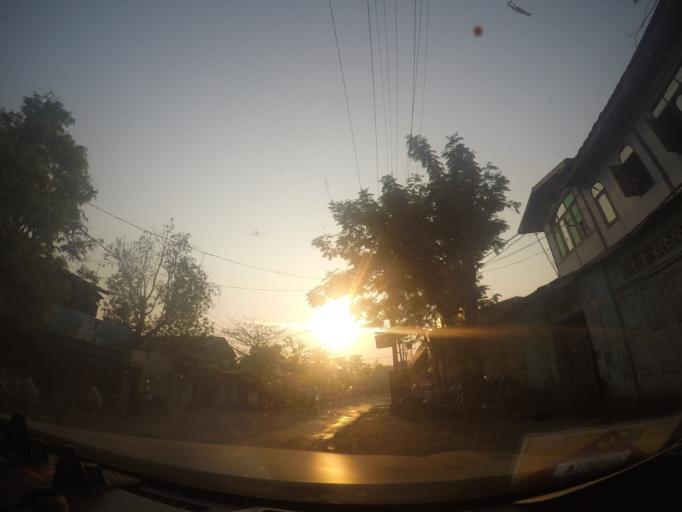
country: MM
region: Bago
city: Pyay
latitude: 18.8253
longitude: 95.2336
